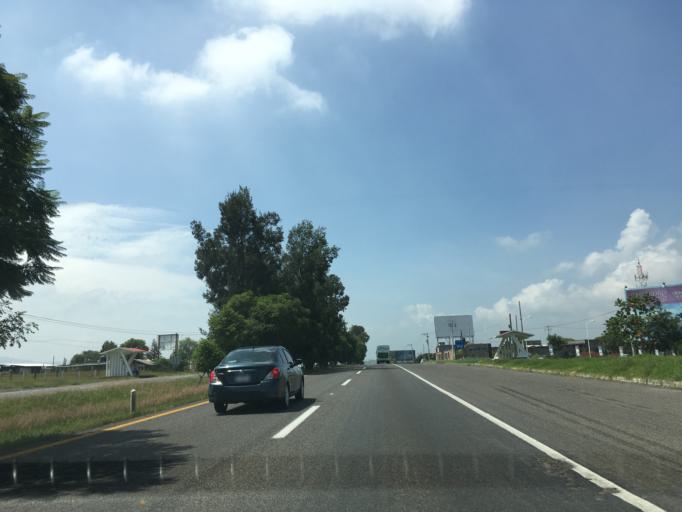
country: MX
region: Michoacan
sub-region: Morelia
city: La Mintzita (Piedra Dura)
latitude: 19.6284
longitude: -101.2762
